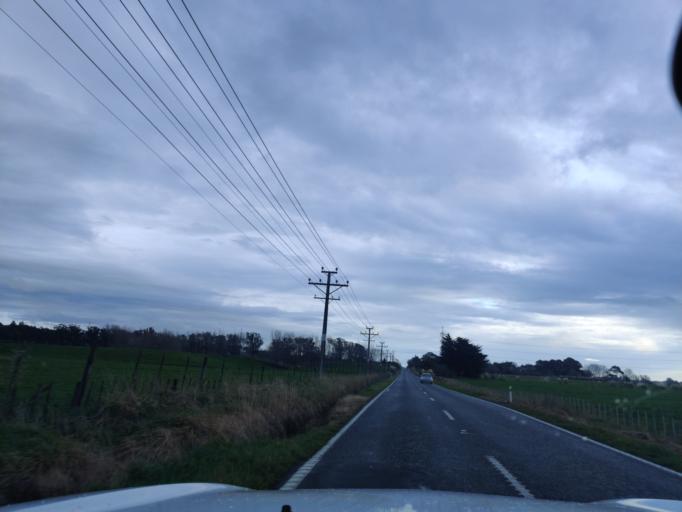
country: NZ
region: Manawatu-Wanganui
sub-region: Palmerston North City
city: Palmerston North
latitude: -40.3411
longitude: 175.7170
